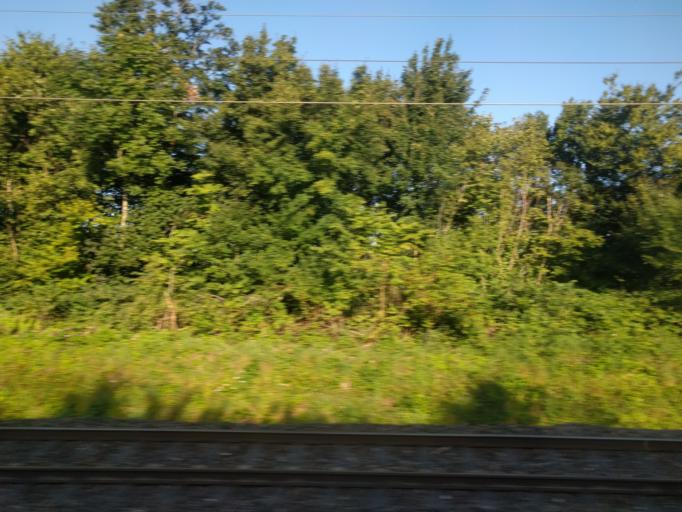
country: DK
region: Zealand
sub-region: Roskilde Kommune
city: Svogerslev
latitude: 55.6127
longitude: 12.0487
